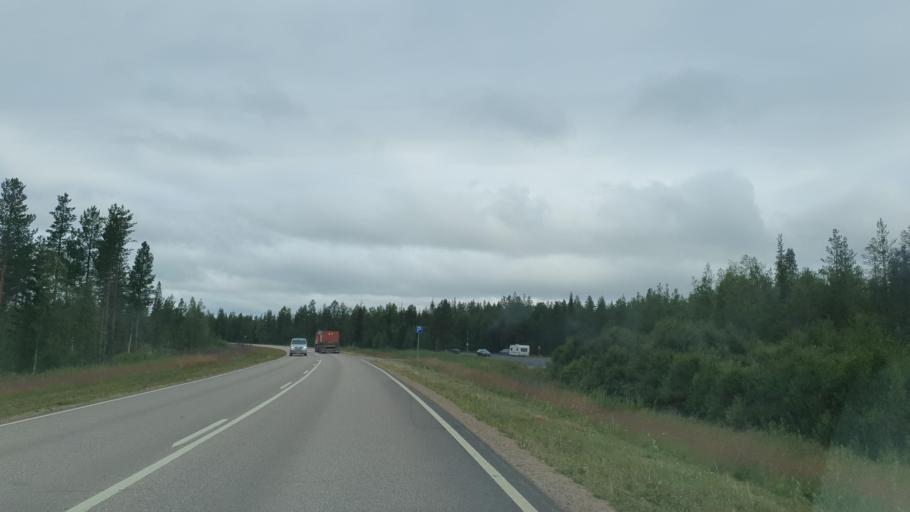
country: FI
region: Lapland
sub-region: Pohjois-Lappi
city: Sodankylae
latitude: 67.4227
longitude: 26.4422
